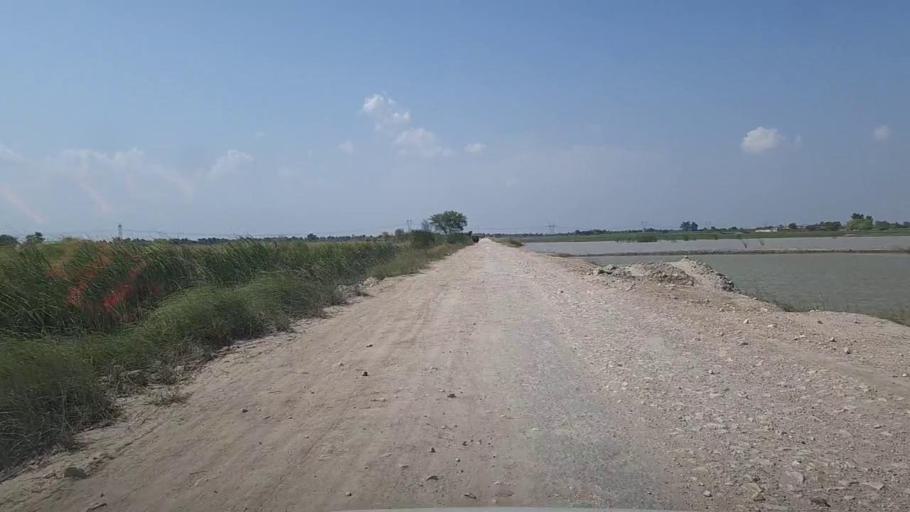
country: PK
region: Sindh
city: Khairpur
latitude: 28.0987
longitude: 69.6268
